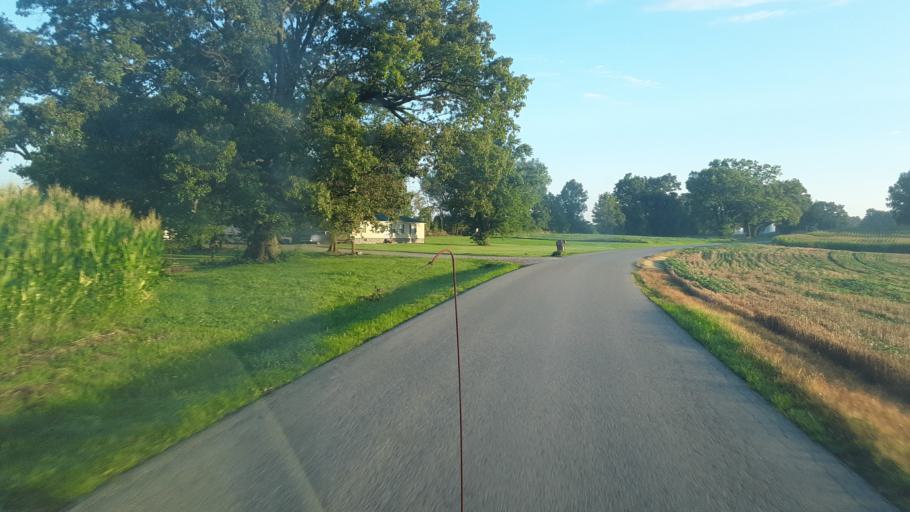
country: US
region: Kentucky
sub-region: Todd County
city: Guthrie
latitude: 36.6866
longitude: -87.1709
